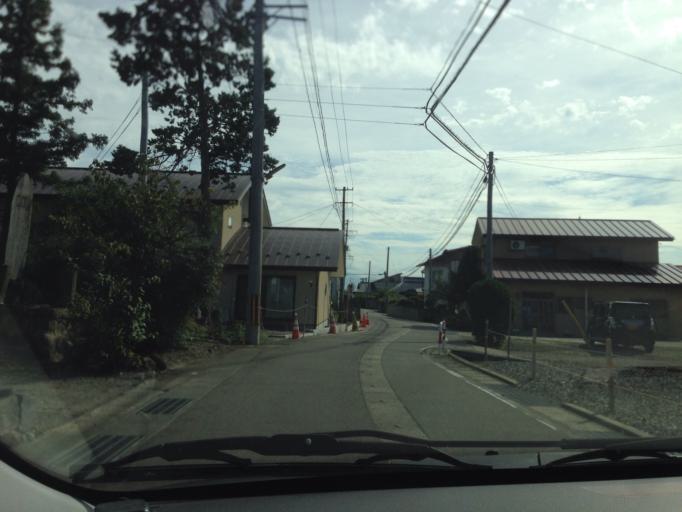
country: JP
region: Fukushima
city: Kitakata
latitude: 37.5999
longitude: 139.9133
